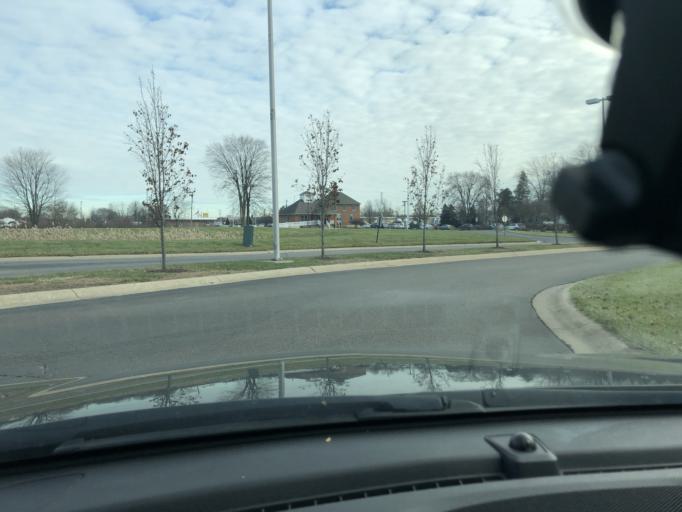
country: US
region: Michigan
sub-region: Wayne County
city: Taylor
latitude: 42.2137
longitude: -83.2405
